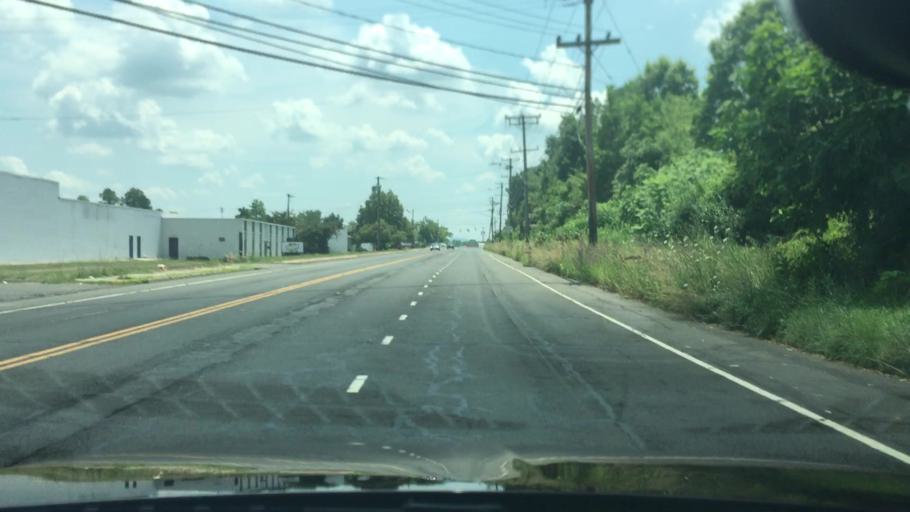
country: US
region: Connecticut
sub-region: Hartford County
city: Kensington
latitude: 41.6567
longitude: -72.7533
